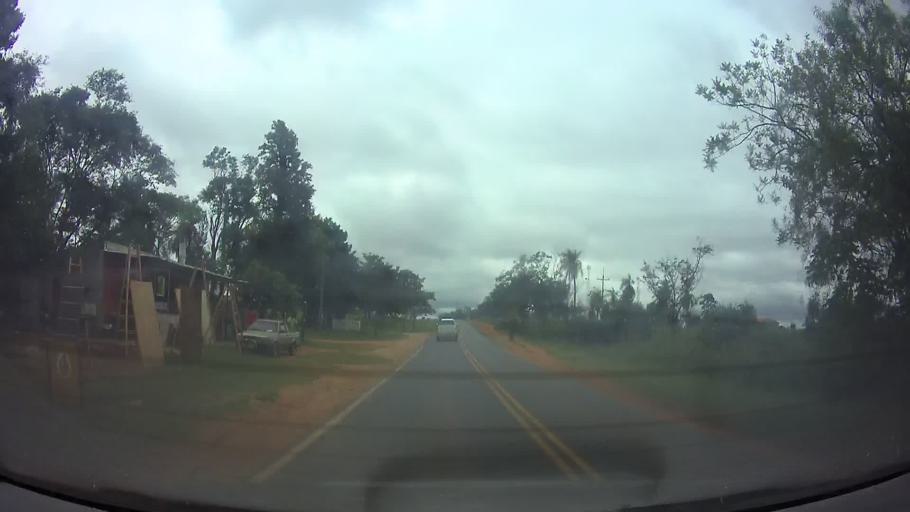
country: PY
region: Central
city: Guarambare
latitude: -25.5268
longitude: -57.4967
